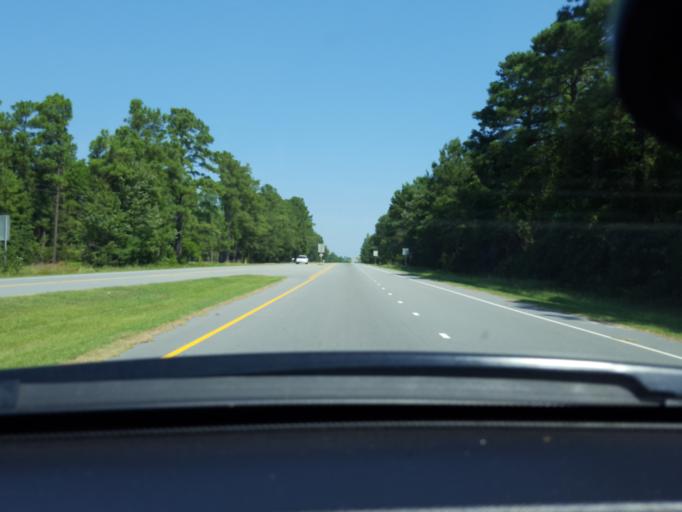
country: US
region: North Carolina
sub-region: Bladen County
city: Elizabethtown
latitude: 34.6577
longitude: -78.4924
